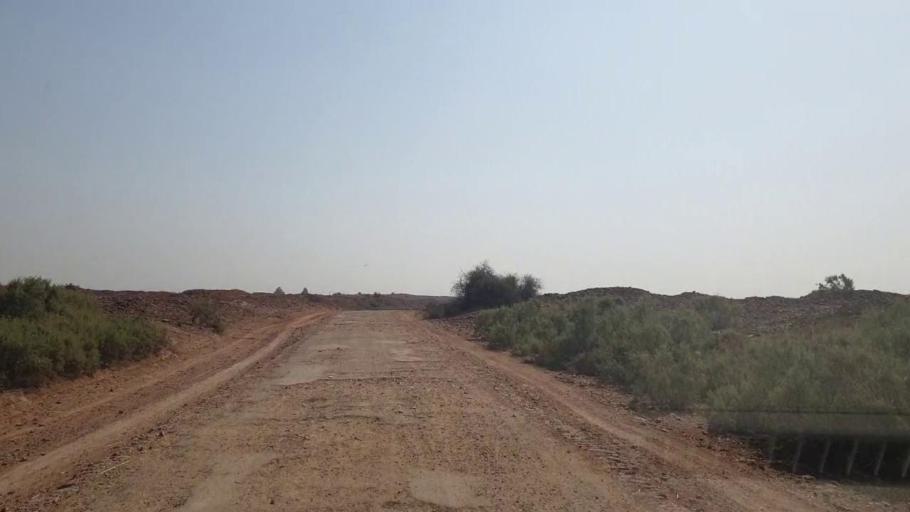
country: PK
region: Sindh
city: Berani
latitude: 25.8820
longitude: 68.7719
